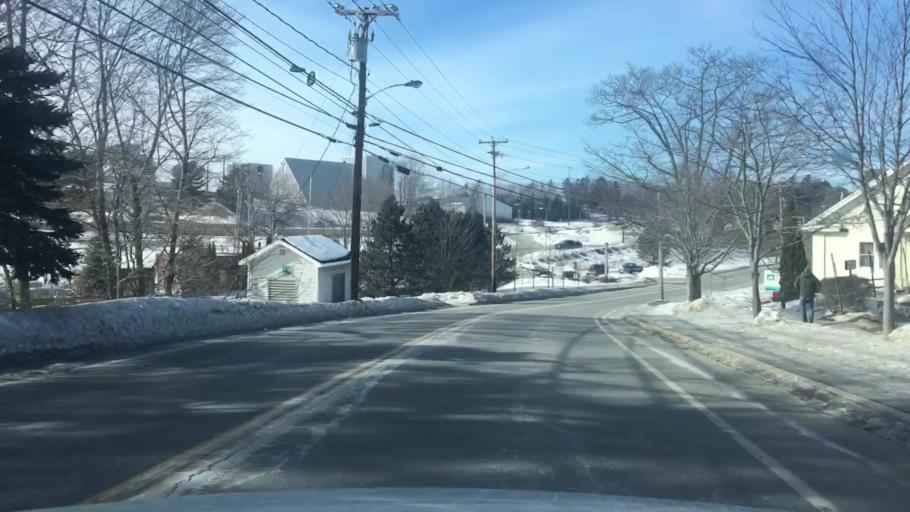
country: US
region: Maine
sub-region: Hancock County
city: Bucksport
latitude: 44.5758
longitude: -68.8025
